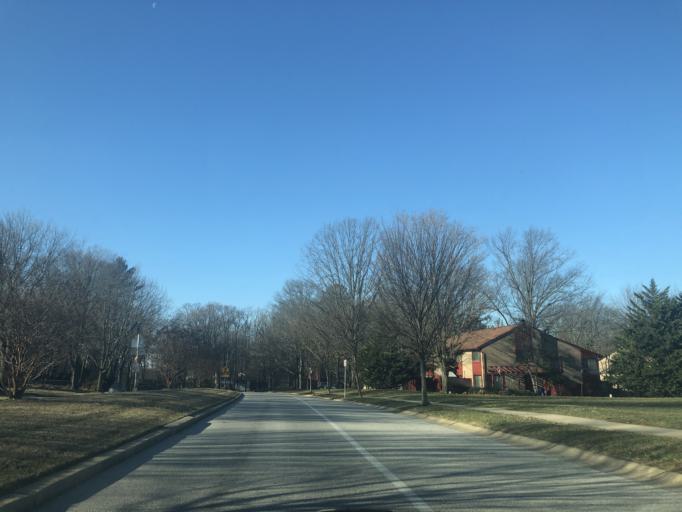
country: US
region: Maryland
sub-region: Howard County
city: Columbia
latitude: 39.2064
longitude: -76.8447
